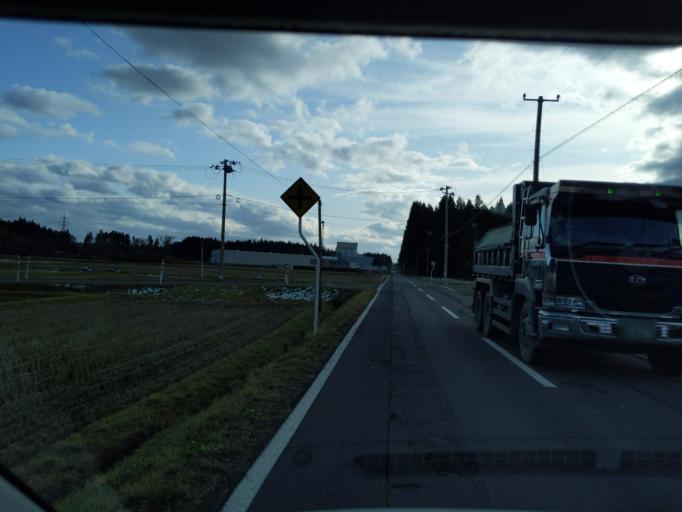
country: JP
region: Iwate
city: Mizusawa
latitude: 39.1100
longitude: 141.0822
